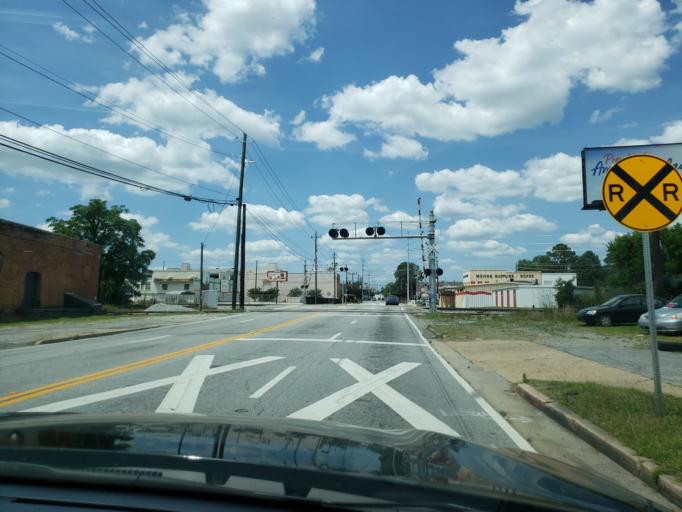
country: US
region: Georgia
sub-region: Muscogee County
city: Columbus
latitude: 32.4630
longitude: -84.9797
